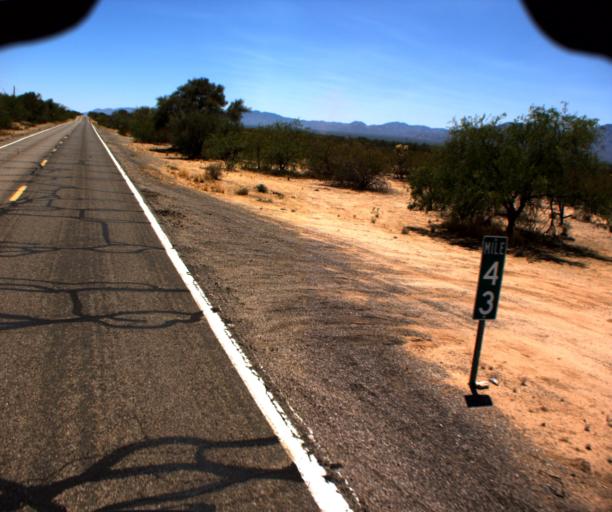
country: US
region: Arizona
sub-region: Pima County
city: Three Points
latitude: 32.0451
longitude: -111.3319
